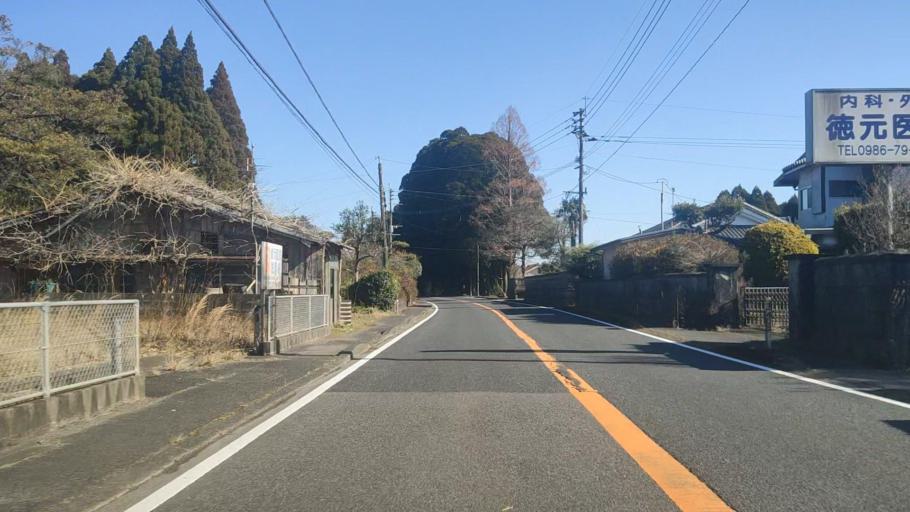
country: JP
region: Kagoshima
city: Sueyoshicho-ninokata
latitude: 31.6848
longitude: 130.9434
